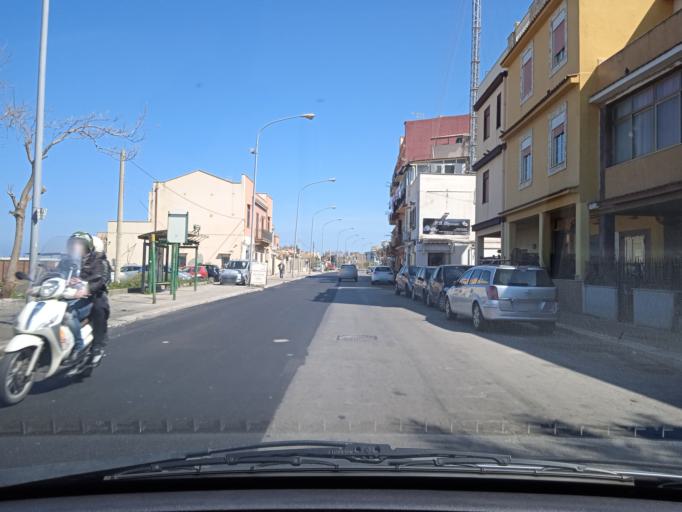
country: IT
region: Sicily
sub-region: Palermo
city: Ciaculli
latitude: 38.0975
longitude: 13.4168
